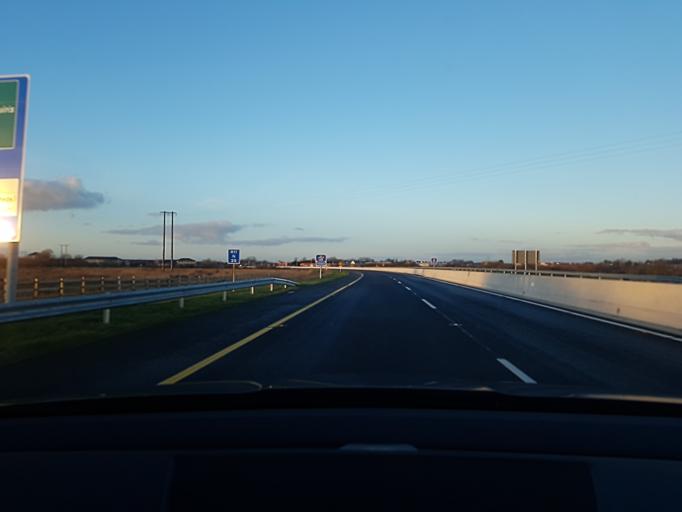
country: IE
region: Connaught
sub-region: County Galway
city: Tuam
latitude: 53.5020
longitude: -8.8783
